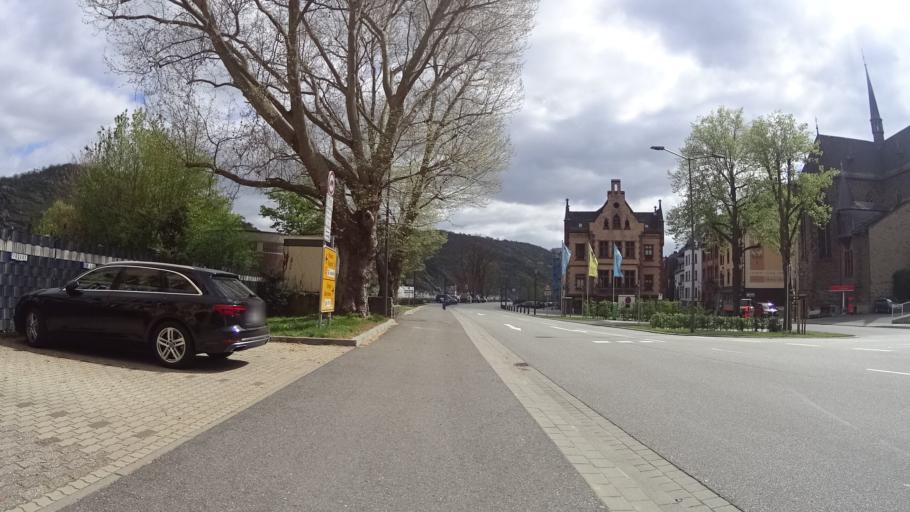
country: DE
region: Rheinland-Pfalz
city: Sankt Goar
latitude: 50.1525
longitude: 7.7104
